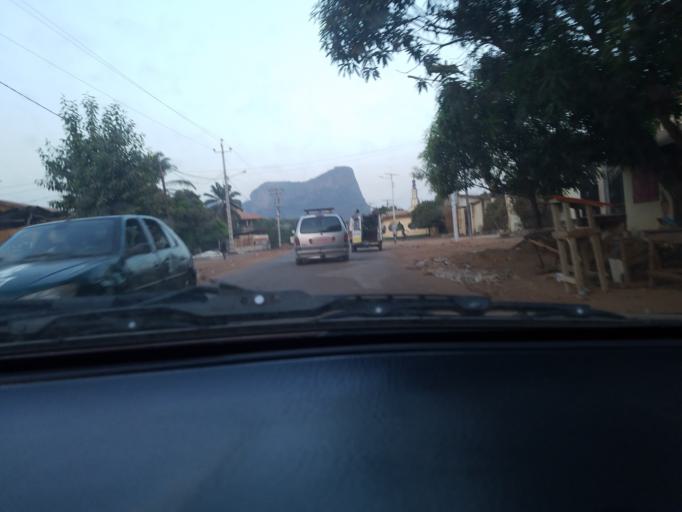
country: GN
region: Kindia
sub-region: Prefecture de Dubreka
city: Dubreka
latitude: 9.7884
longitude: -13.4986
